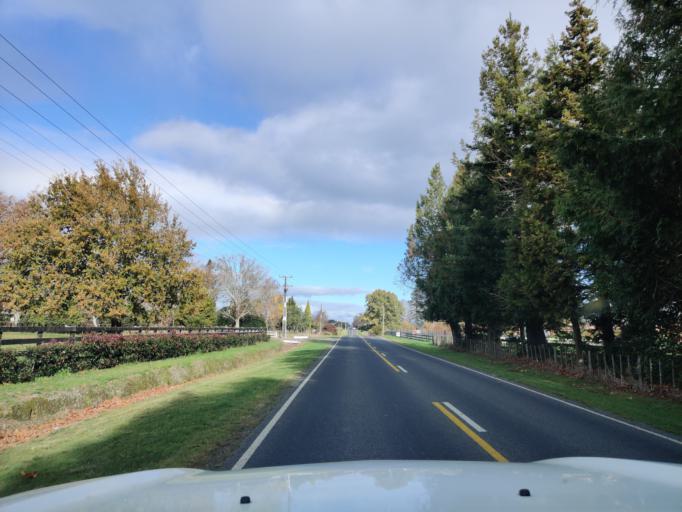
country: NZ
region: Waikato
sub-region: Waipa District
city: Cambridge
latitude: -37.8508
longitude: 175.4391
